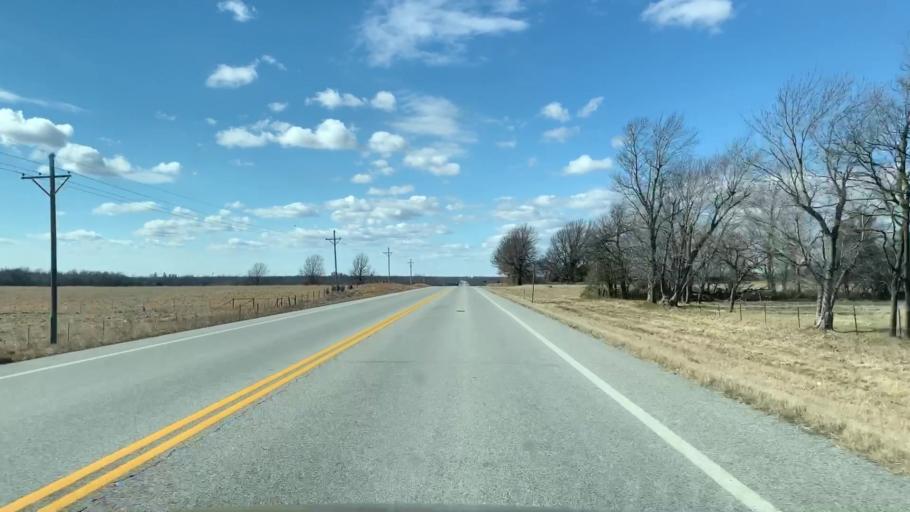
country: US
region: Kansas
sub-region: Cherokee County
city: Columbus
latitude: 37.1781
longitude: -94.7856
